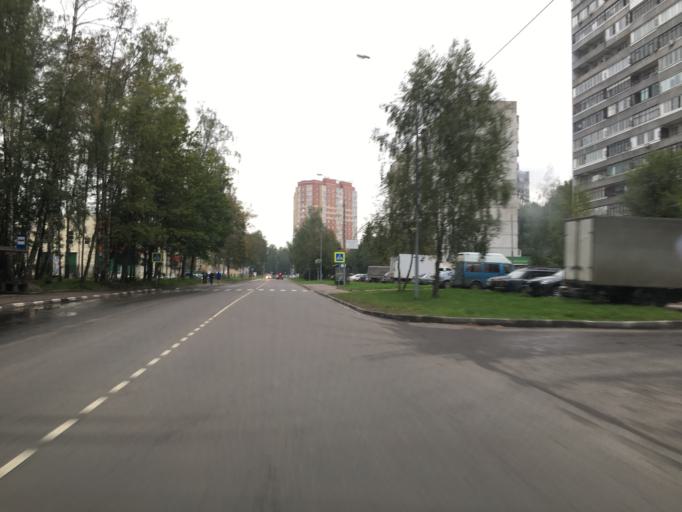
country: RU
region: Moskovskaya
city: Troitsk
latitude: 55.4688
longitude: 37.2916
